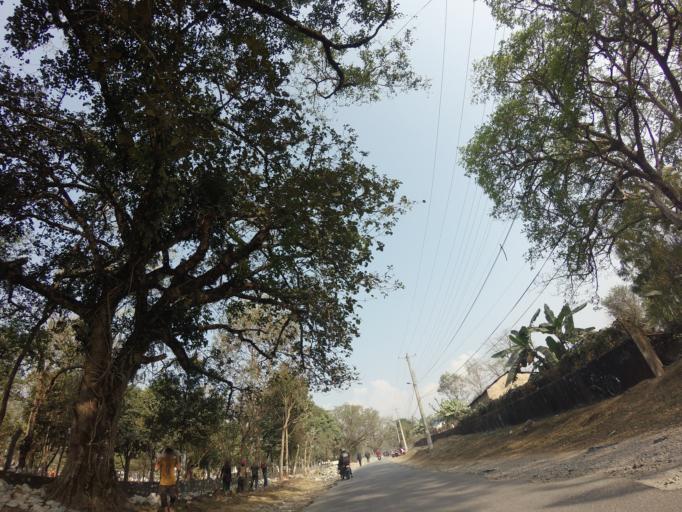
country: NP
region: Western Region
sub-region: Gandaki Zone
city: Pokhara
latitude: 28.2026
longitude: 83.9712
